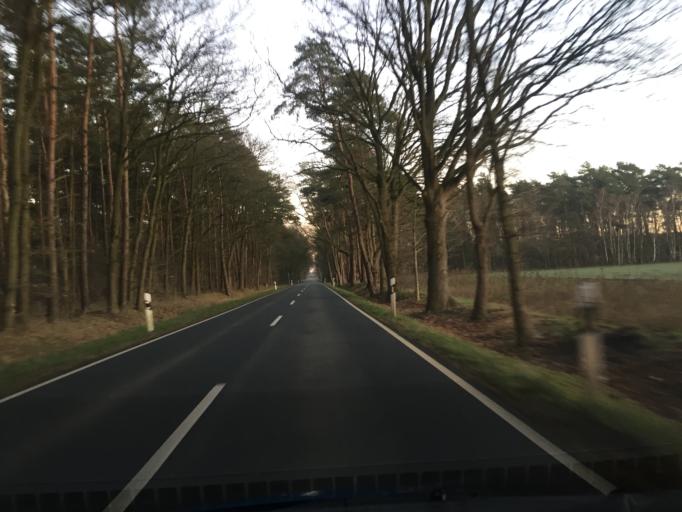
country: DE
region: Lower Saxony
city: Adelheidsdorf
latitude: 52.5224
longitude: 10.0509
